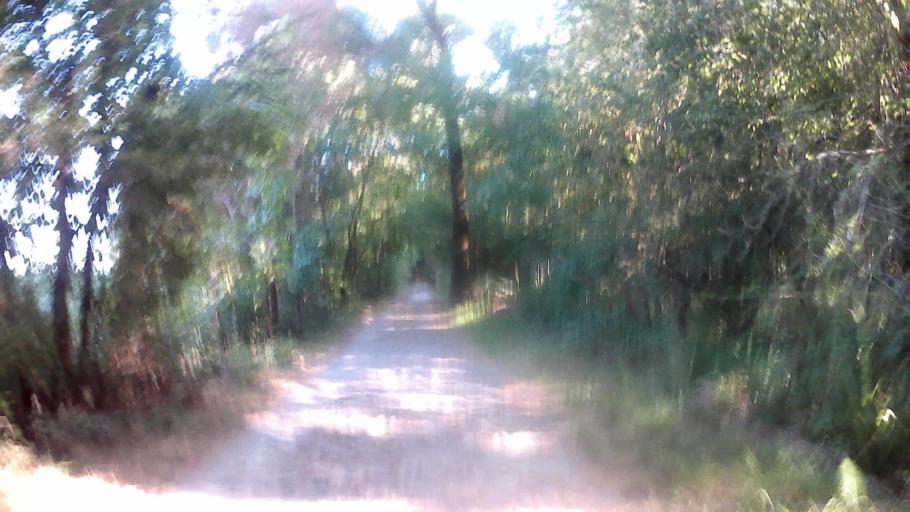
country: FR
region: Aquitaine
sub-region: Departement de la Gironde
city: Begles
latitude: 44.7964
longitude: -0.5283
